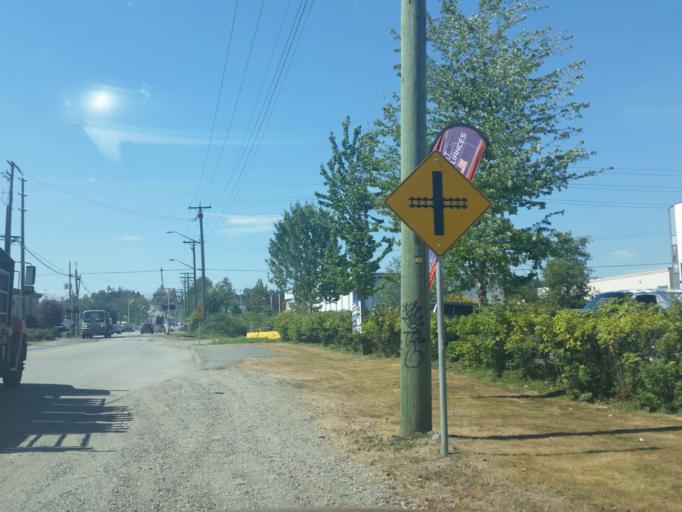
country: CA
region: British Columbia
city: Langley
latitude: 49.1045
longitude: -122.6826
